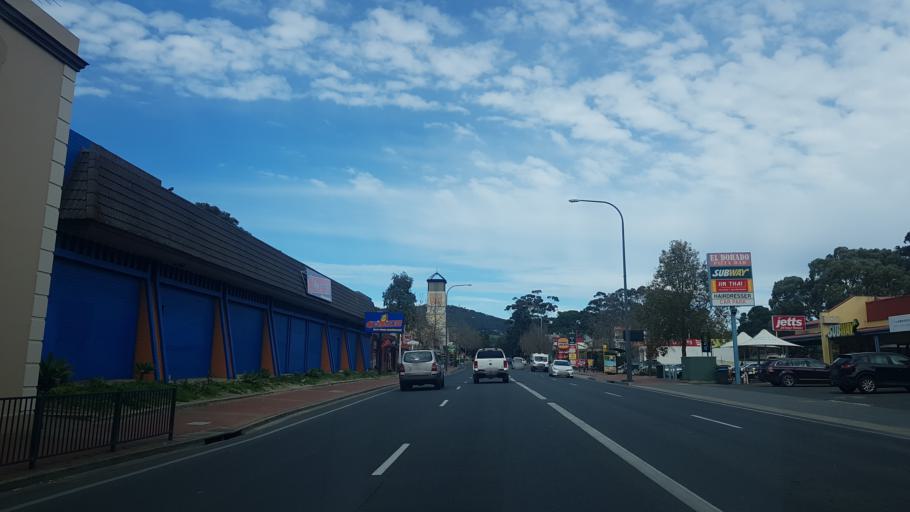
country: AU
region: South Australia
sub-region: Mitcham
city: Hawthorn
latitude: -34.9743
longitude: 138.6093
